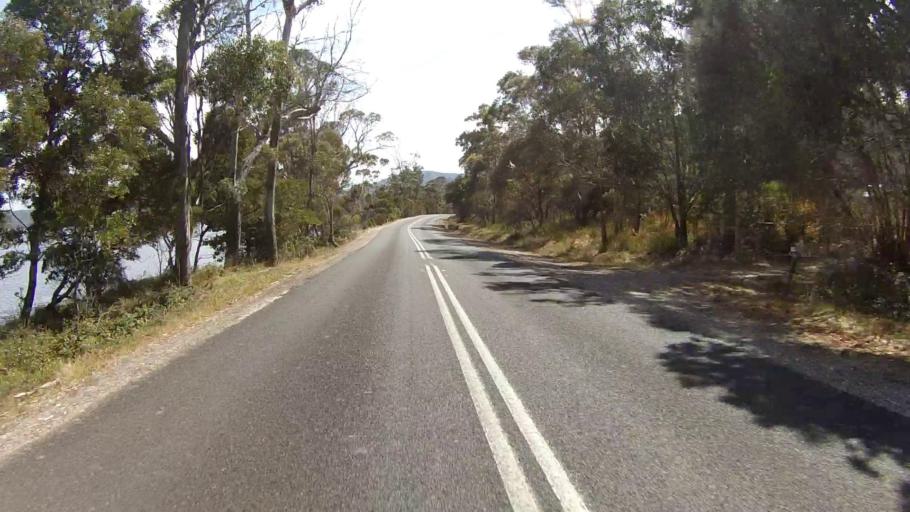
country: AU
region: Tasmania
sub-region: Huon Valley
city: Cygnet
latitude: -43.2646
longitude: 147.1428
